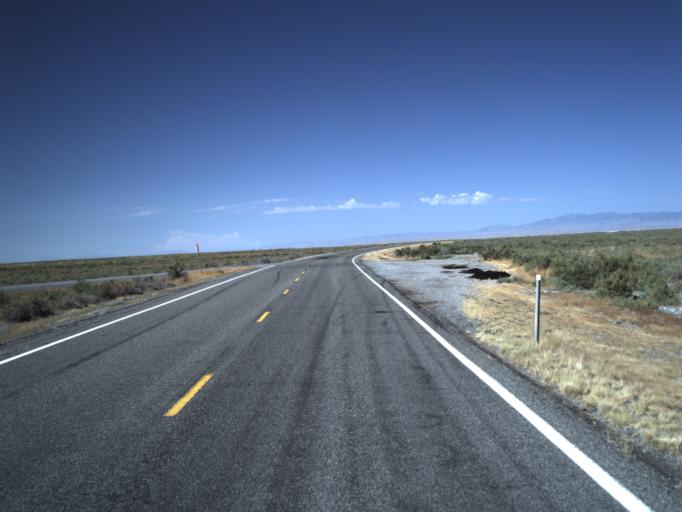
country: US
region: Utah
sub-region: Millard County
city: Delta
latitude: 39.3170
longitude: -112.7477
